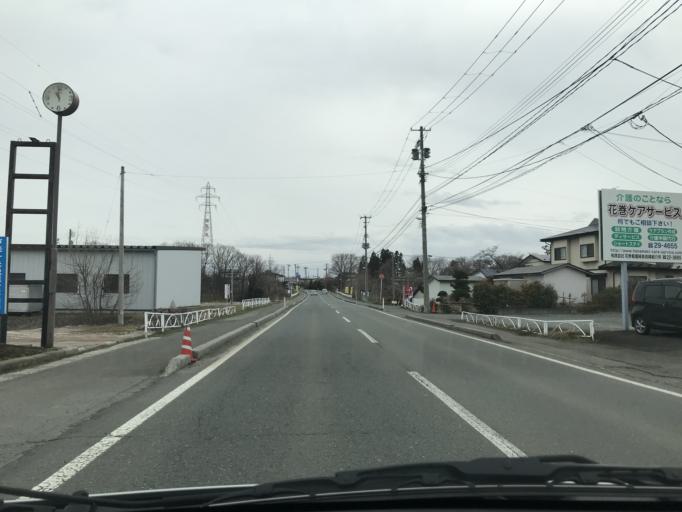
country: JP
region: Iwate
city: Hanamaki
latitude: 39.4105
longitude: 141.1083
